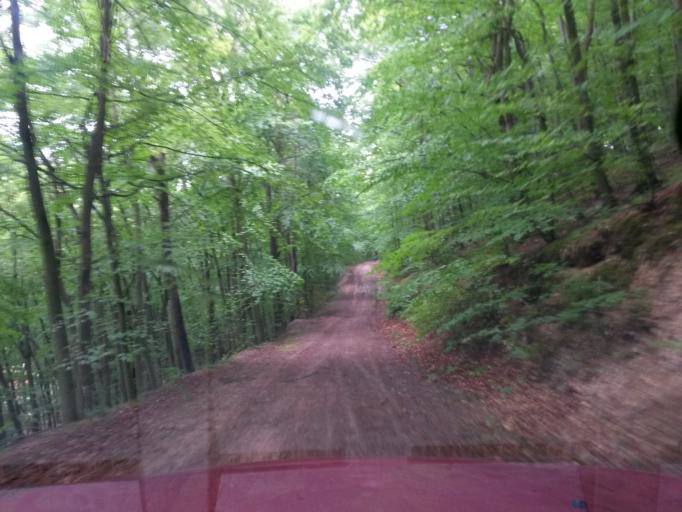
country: SK
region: Kosicky
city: Kosice
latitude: 48.7229
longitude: 21.1658
